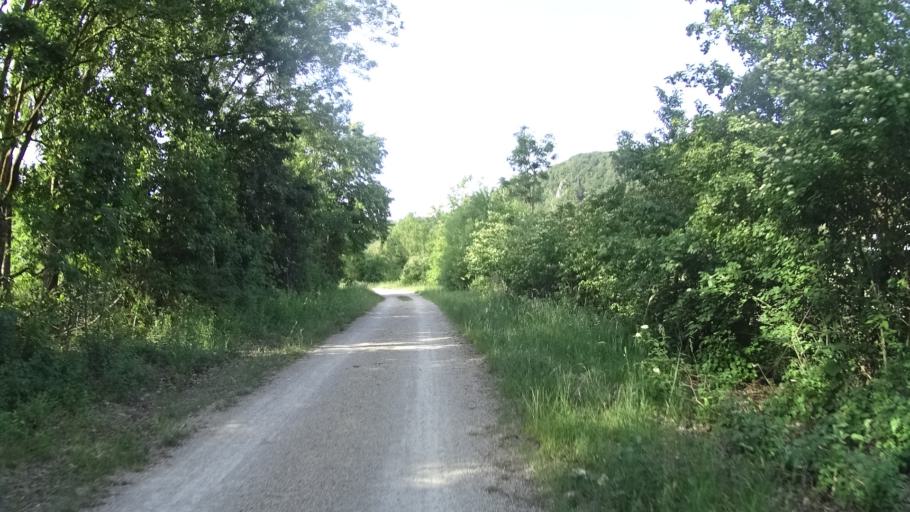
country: DE
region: Bavaria
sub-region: Lower Bavaria
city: Riedenburg
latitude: 48.9686
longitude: 11.6832
